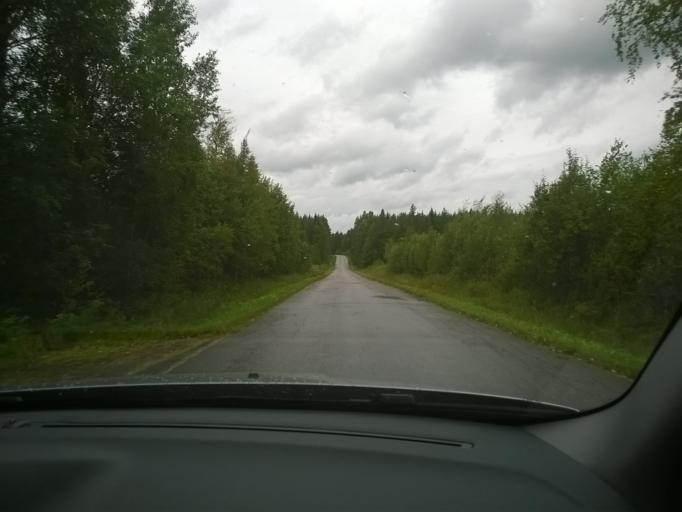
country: FI
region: Kainuu
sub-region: Kehys-Kainuu
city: Kuhmo
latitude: 64.1315
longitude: 29.4432
